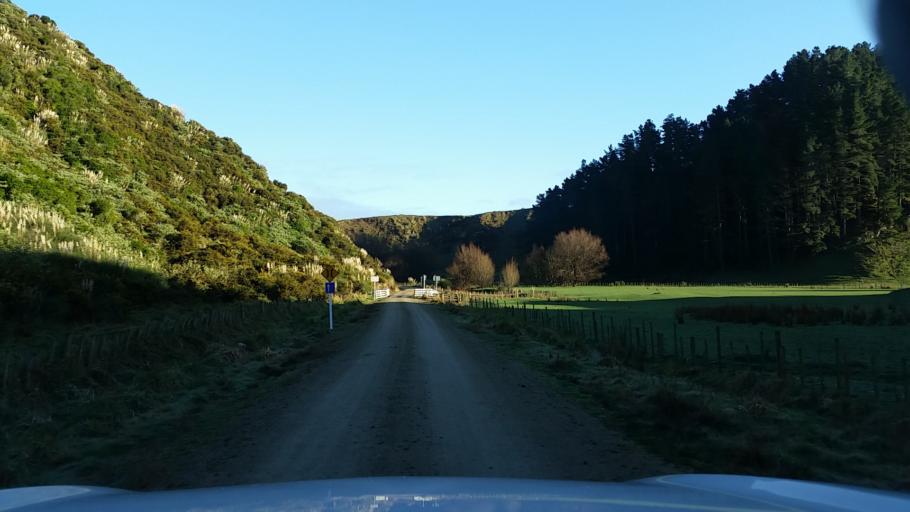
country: NZ
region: Taranaki
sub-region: South Taranaki District
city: Patea
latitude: -39.7608
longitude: 174.7355
